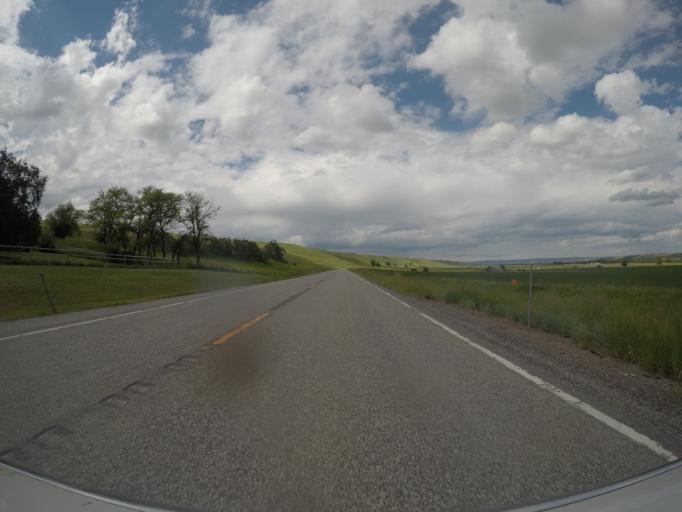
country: US
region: Montana
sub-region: Sweet Grass County
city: Big Timber
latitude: 45.7667
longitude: -109.9899
